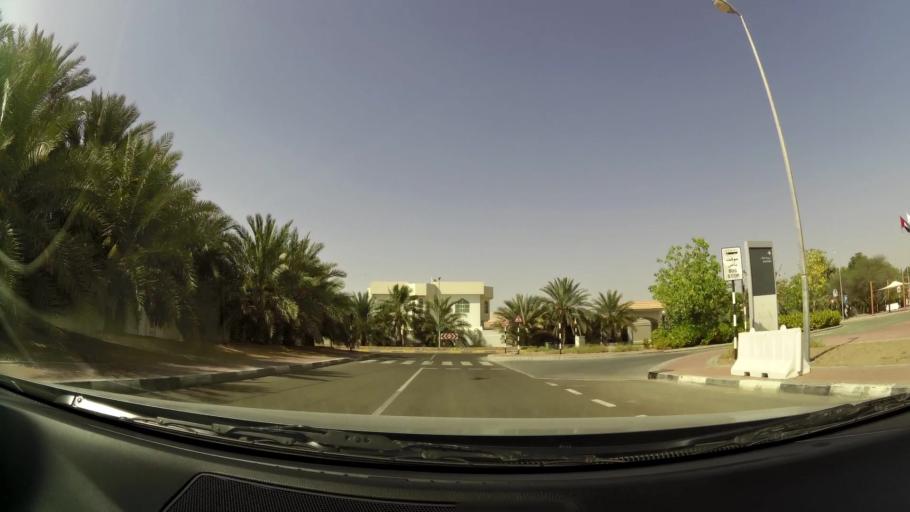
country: OM
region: Al Buraimi
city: Al Buraymi
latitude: 24.3119
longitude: 55.8014
